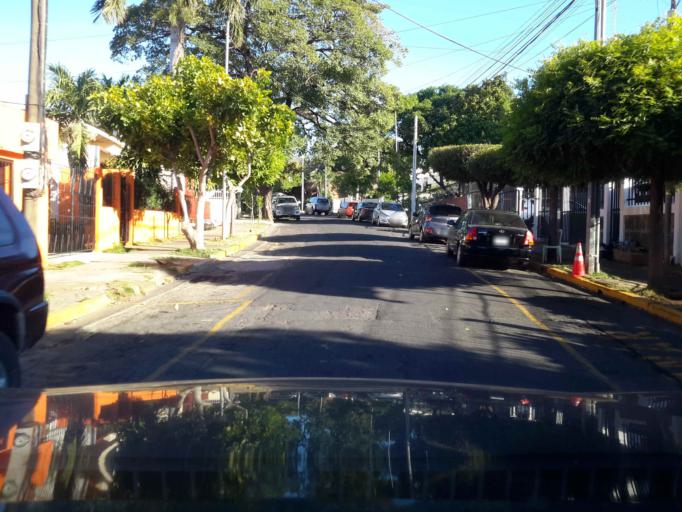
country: NI
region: Managua
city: Managua
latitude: 12.1408
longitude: -86.2782
